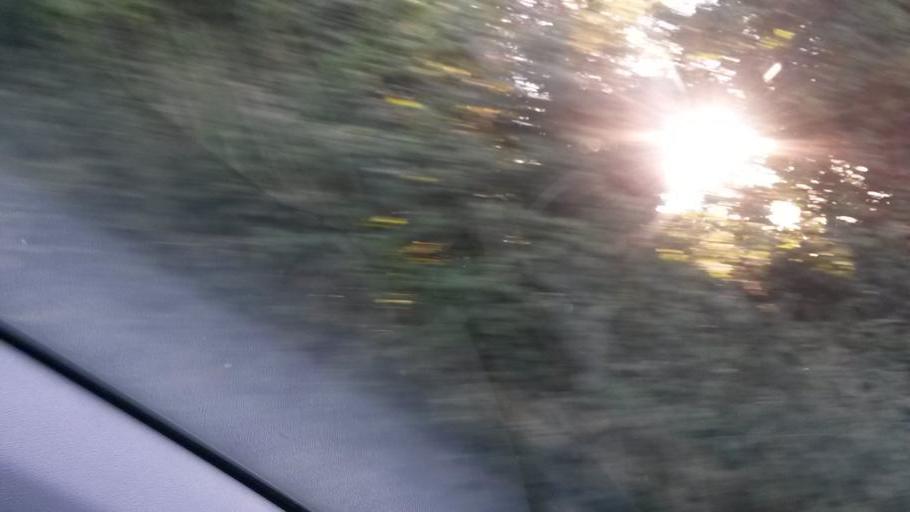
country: IE
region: Leinster
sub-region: An Mhi
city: Ashbourne
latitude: 53.5663
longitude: -6.3785
